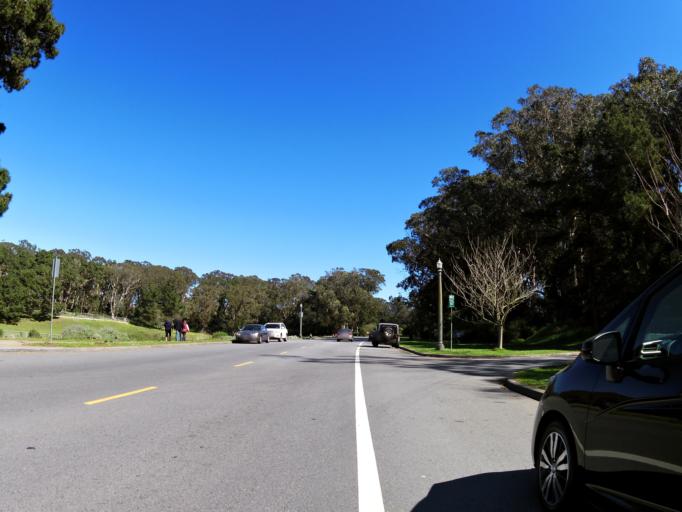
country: US
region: California
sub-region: San Mateo County
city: Daly City
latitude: 37.7688
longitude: -122.4983
